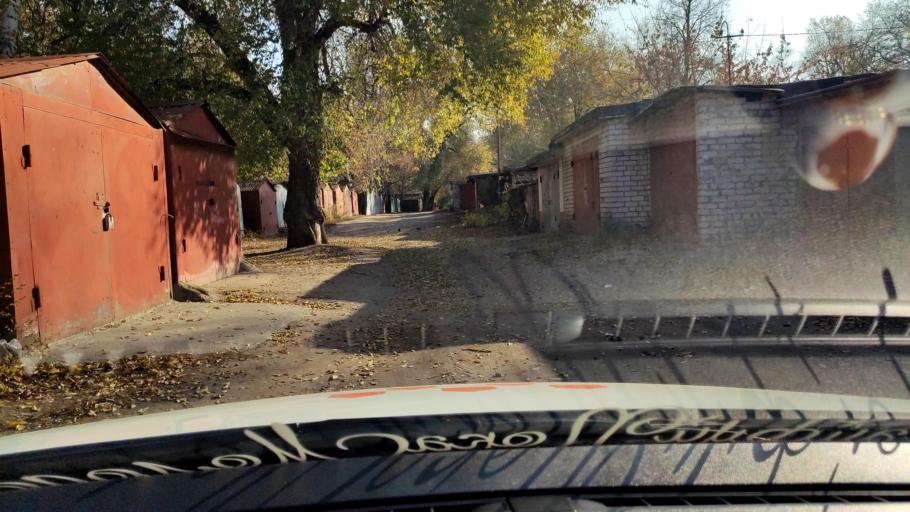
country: RU
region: Voronezj
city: Voronezh
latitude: 51.6764
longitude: 39.1444
